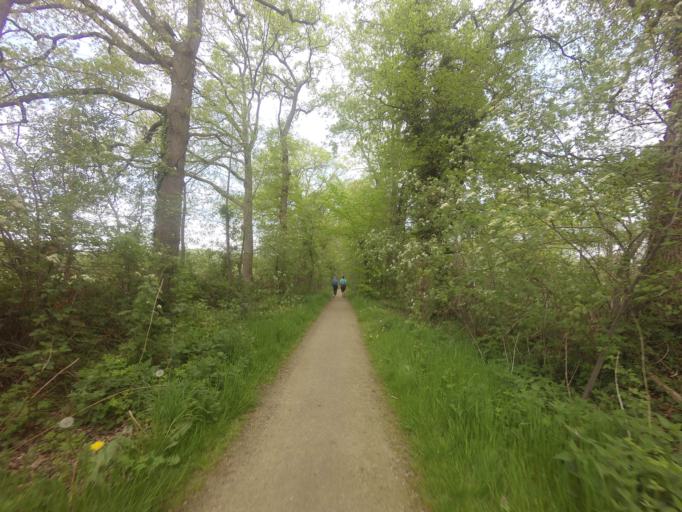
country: NL
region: Overijssel
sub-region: Gemeente Hof van Twente
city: Delden
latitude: 52.2184
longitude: 6.7339
